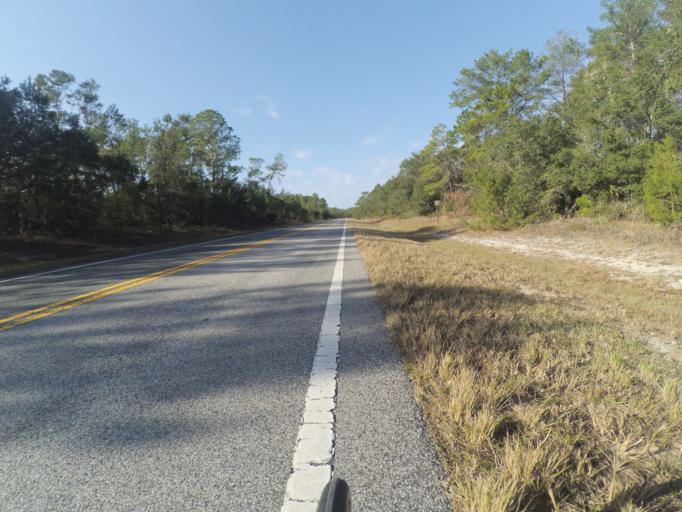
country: US
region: Florida
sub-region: Lake County
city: Astor
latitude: 29.1438
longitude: -81.5821
